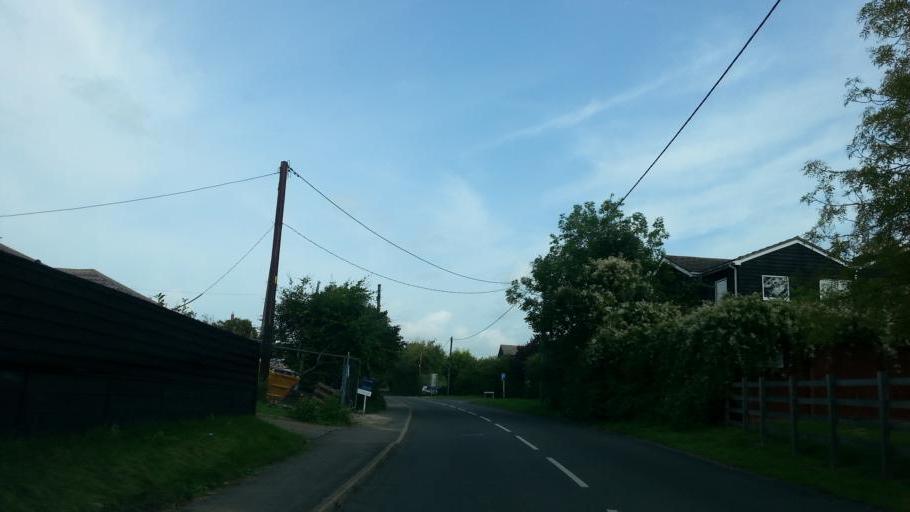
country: GB
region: England
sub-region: Cambridgeshire
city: Comberton
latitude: 52.2104
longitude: 0.0120
